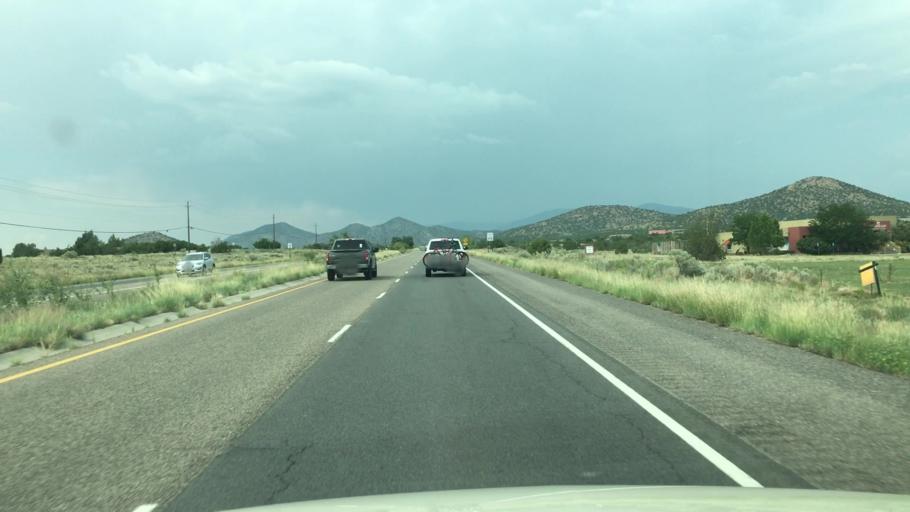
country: US
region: New Mexico
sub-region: Santa Fe County
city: Eldorado at Santa Fe
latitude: 35.5229
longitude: -105.8920
